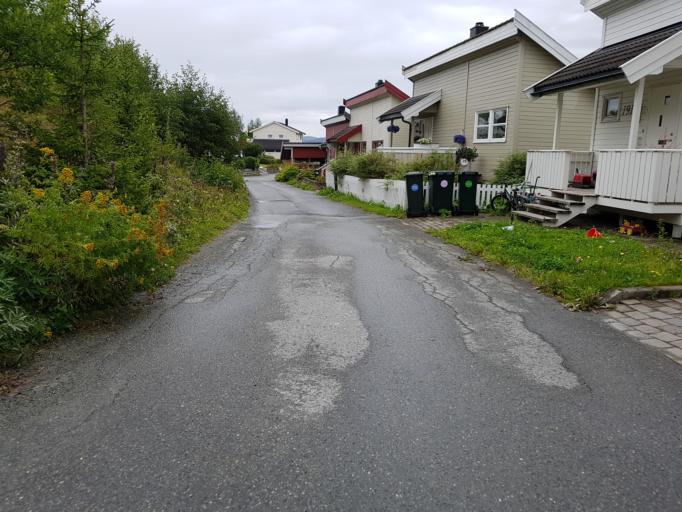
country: NO
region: Sor-Trondelag
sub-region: Trondheim
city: Trondheim
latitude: 63.3839
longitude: 10.3428
